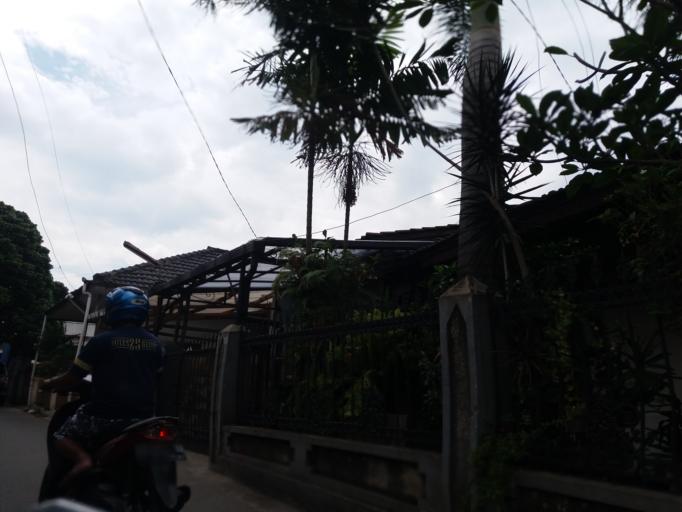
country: ID
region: West Java
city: Bandung
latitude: -6.9266
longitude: 107.6541
